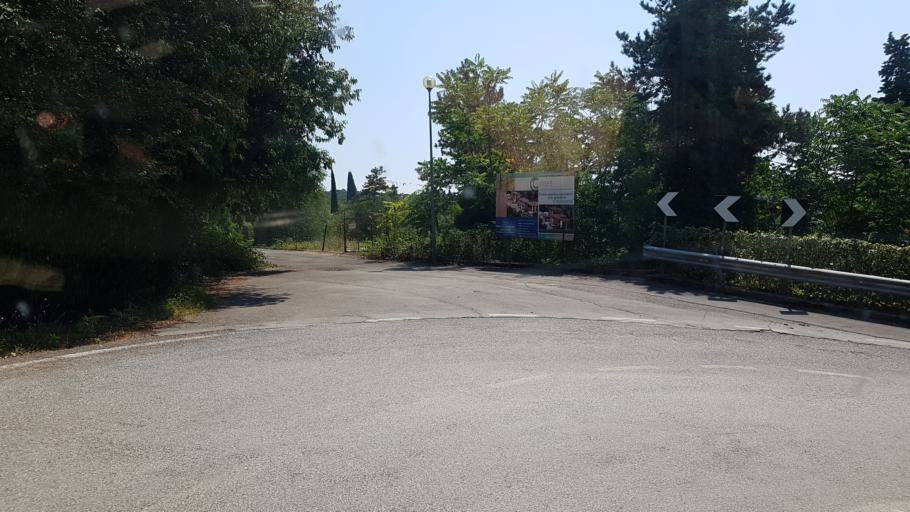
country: IT
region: Friuli Venezia Giulia
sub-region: Provincia di Gorizia
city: Sagrado
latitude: 45.8753
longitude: 13.4902
